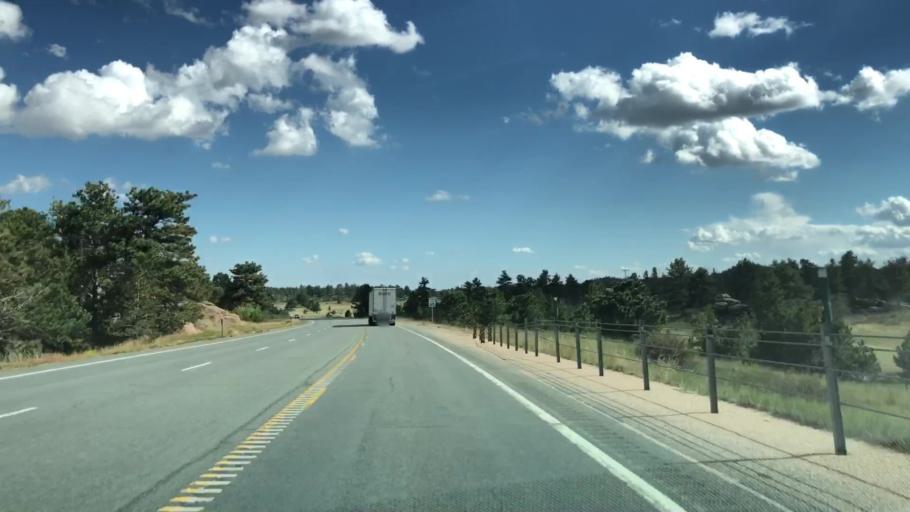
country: US
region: Wyoming
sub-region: Albany County
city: Laramie
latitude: 40.9912
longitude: -105.4100
